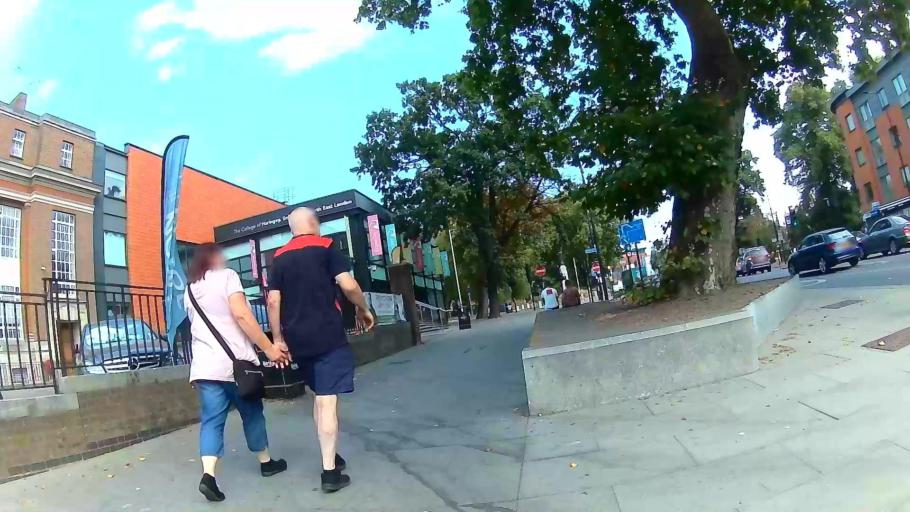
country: GB
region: England
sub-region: Greater London
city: Harringay
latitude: 51.5861
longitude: -0.0718
